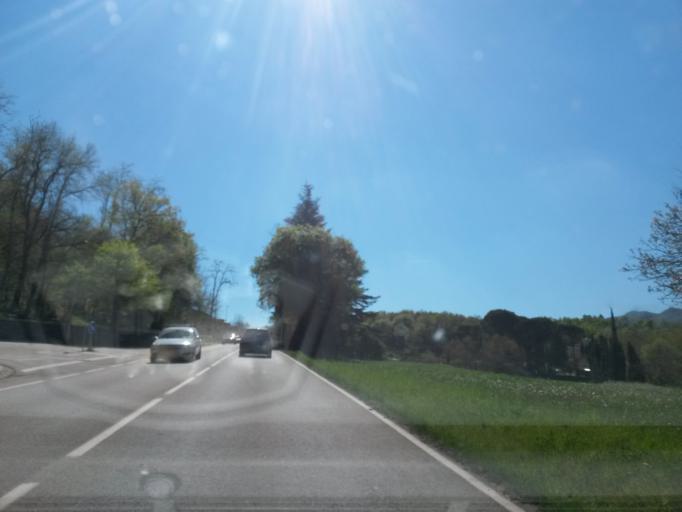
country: ES
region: Catalonia
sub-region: Provincia de Girona
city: Sant Cristofol de les Fonts
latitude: 42.1711
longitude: 2.4990
